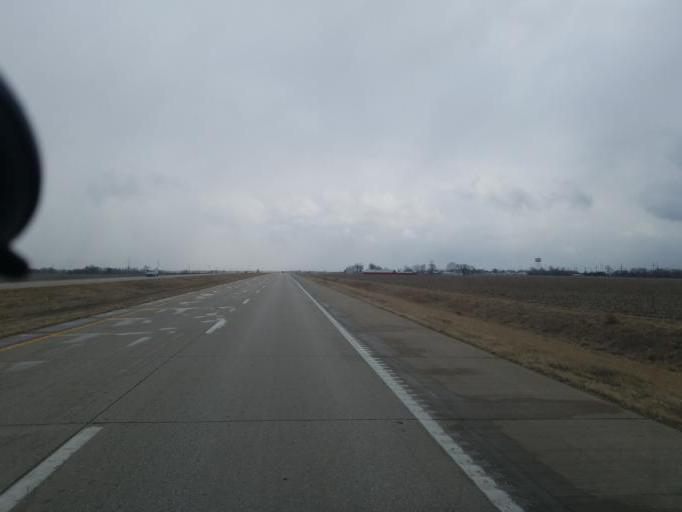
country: US
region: Missouri
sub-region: Randolph County
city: Moberly
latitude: 39.5292
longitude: -92.4433
